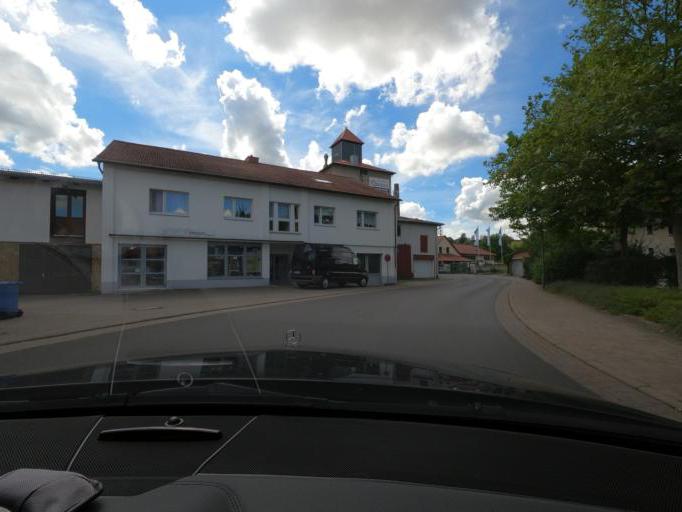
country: DE
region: Hesse
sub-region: Regierungsbezirk Kassel
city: Sontra
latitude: 51.0699
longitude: 9.9330
